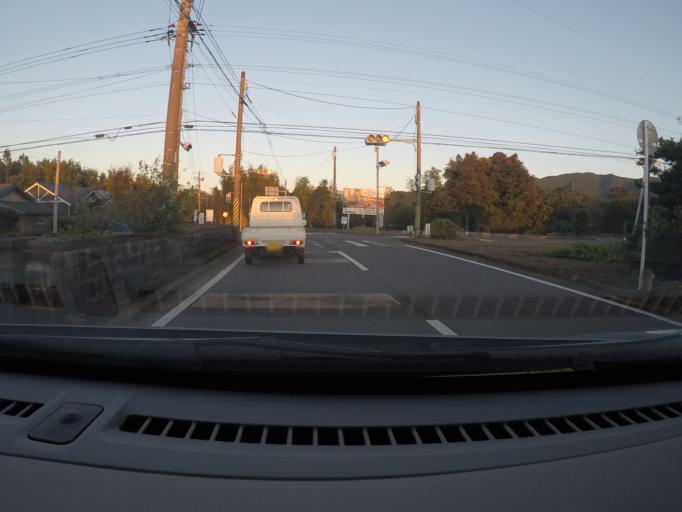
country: JP
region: Kagoshima
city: Izumi
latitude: 32.0538
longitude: 130.3357
